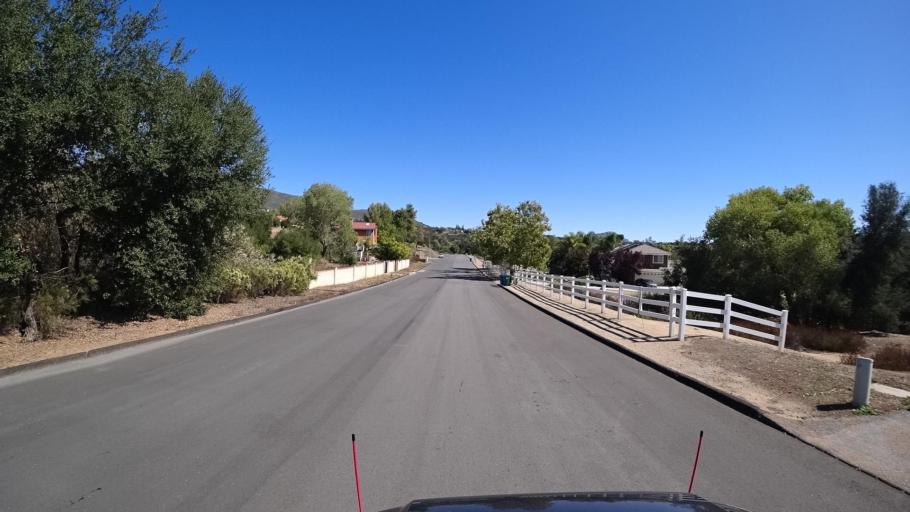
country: US
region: California
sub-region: San Diego County
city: Alpine
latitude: 32.8399
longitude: -116.7632
